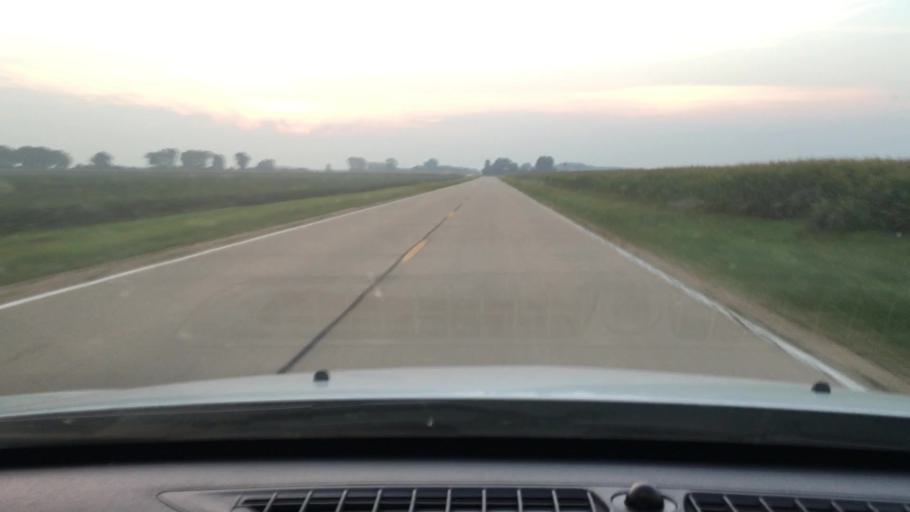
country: US
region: Illinois
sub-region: Ogle County
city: Rochelle
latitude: 41.8468
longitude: -89.0606
